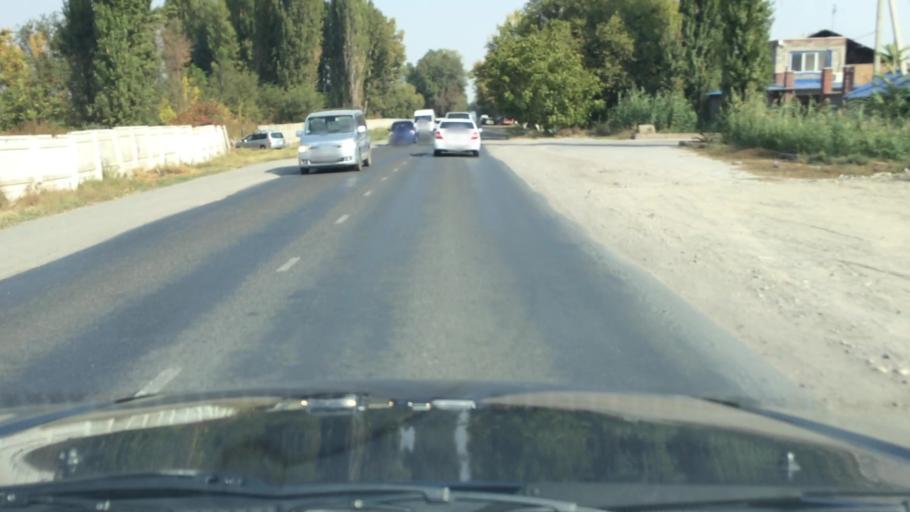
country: KG
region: Chuy
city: Lebedinovka
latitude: 42.8936
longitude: 74.6810
